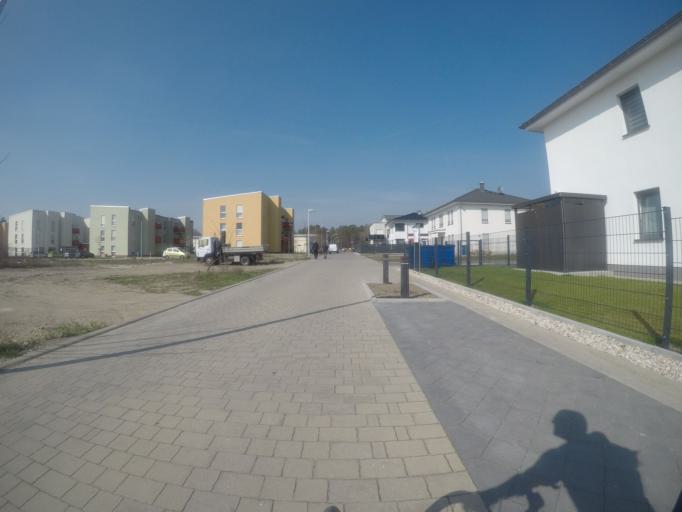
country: DE
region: Brandenburg
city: Konigs Wusterhausen
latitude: 52.2953
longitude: 13.6843
